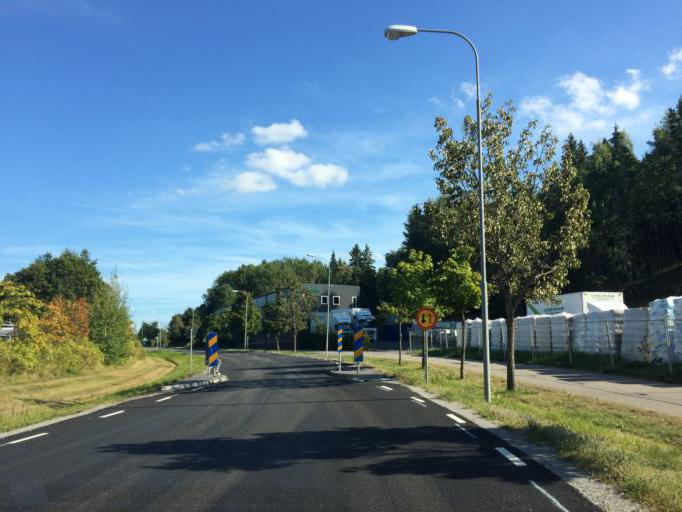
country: SE
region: Stockholm
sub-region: Upplands Vasby Kommun
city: Upplands Vaesby
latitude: 59.4965
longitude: 17.9338
